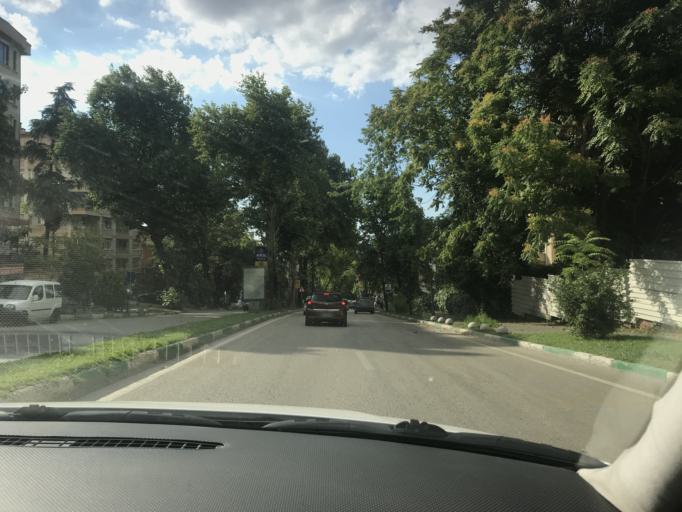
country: TR
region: Bursa
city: Yildirim
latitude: 40.2051
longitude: 29.0198
